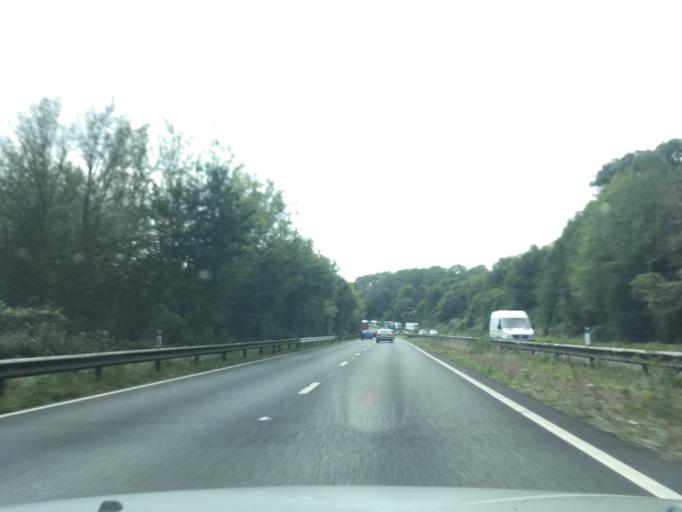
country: GB
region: England
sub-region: Hampshire
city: Petersfield
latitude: 50.9572
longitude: -0.9803
